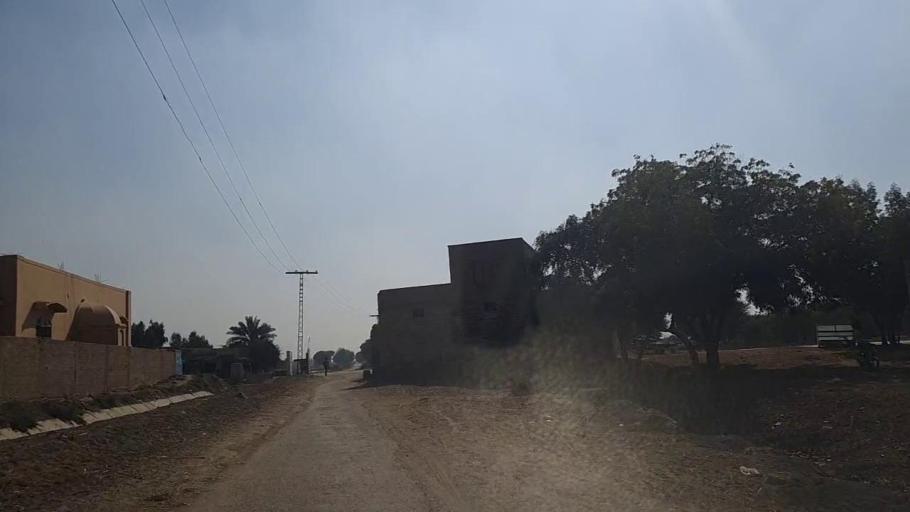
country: PK
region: Sindh
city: Shahpur Chakar
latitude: 26.1889
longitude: 68.5835
